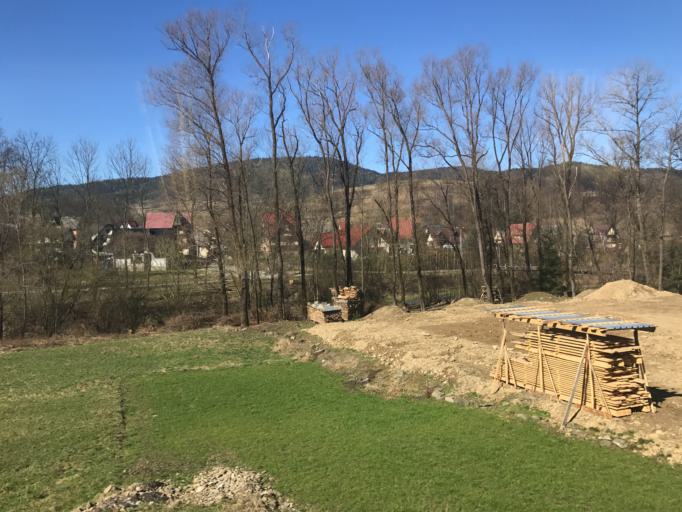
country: PL
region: Lesser Poland Voivodeship
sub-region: Powiat myslenicki
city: Lubien
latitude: 49.7049
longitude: 19.9676
